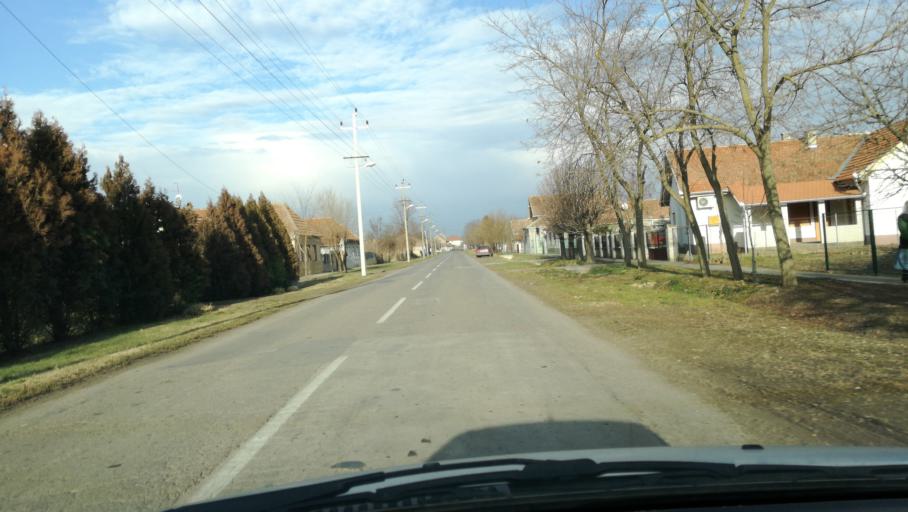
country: RS
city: Rusko Selo
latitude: 45.7651
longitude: 20.5868
